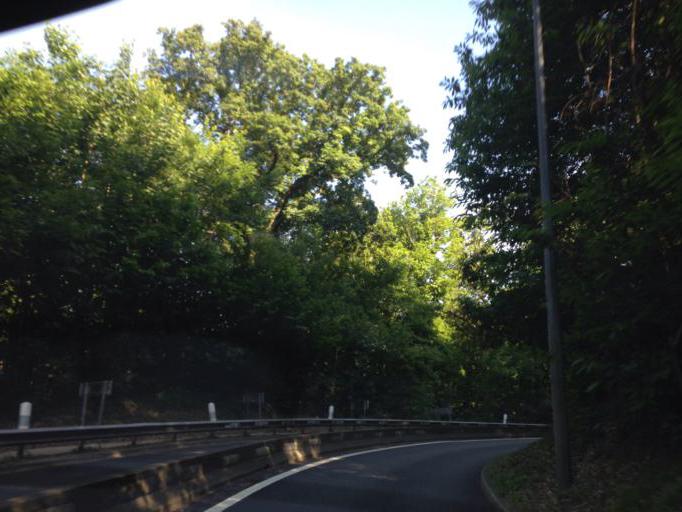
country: FR
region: Ile-de-France
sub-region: Departement des Hauts-de-Seine
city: Meudon
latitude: 48.7911
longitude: 2.2324
